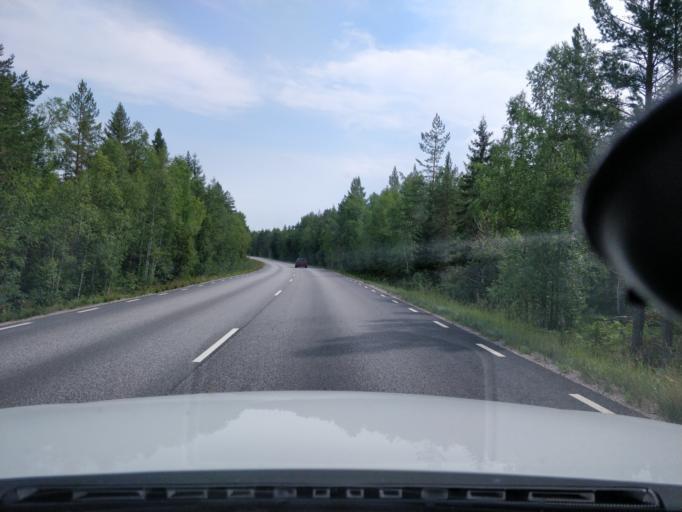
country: SE
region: Dalarna
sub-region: Ludvika Kommun
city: Ludvika
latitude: 60.2903
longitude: 15.2405
